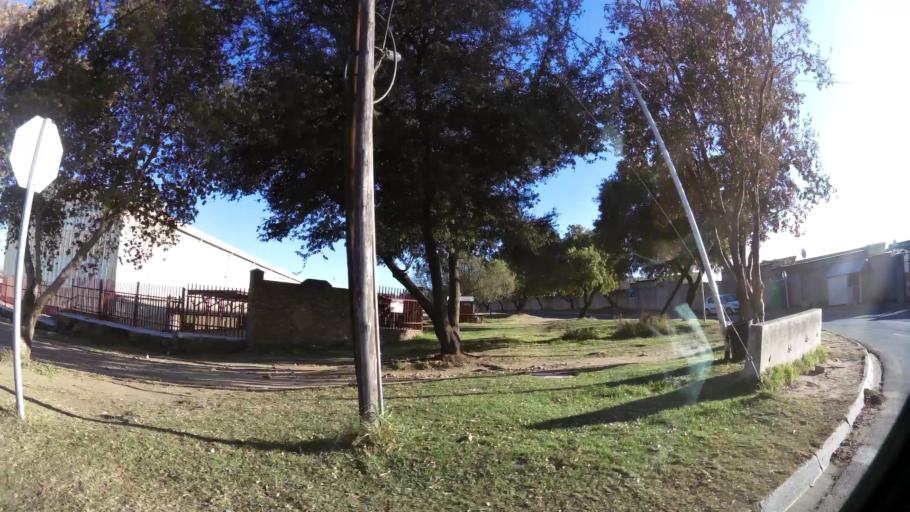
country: ZA
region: Gauteng
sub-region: City of Johannesburg Metropolitan Municipality
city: Modderfontein
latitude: -26.0375
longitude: 28.1595
